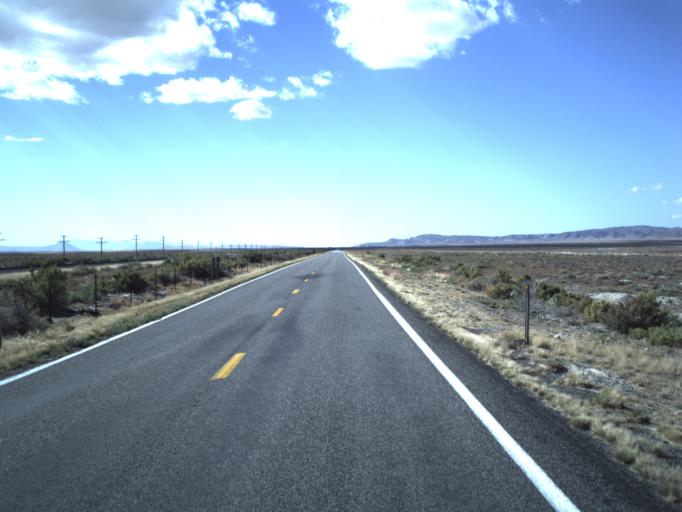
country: US
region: Utah
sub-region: Millard County
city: Delta
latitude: 39.0479
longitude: -112.7685
